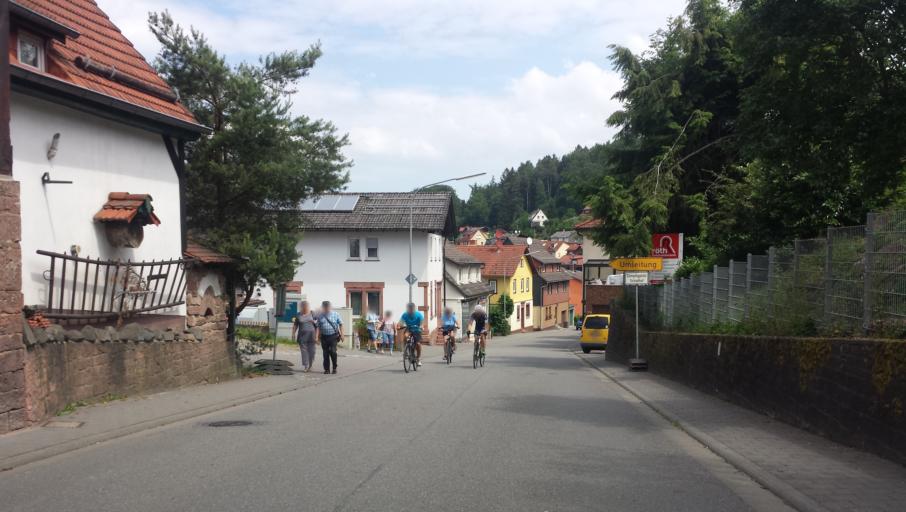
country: DE
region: Hesse
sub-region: Regierungsbezirk Darmstadt
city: Furth
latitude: 49.6369
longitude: 8.8331
